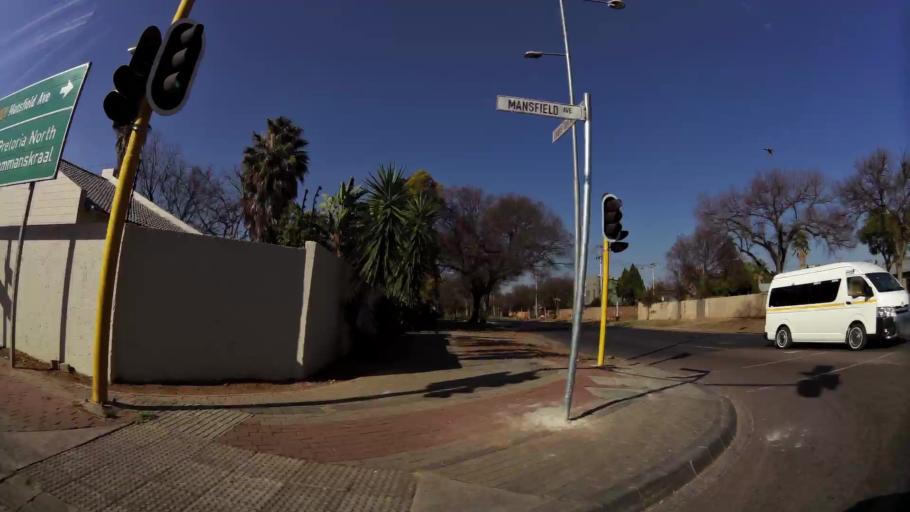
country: ZA
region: Gauteng
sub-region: City of Tshwane Metropolitan Municipality
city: Pretoria
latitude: -25.7054
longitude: 28.1871
